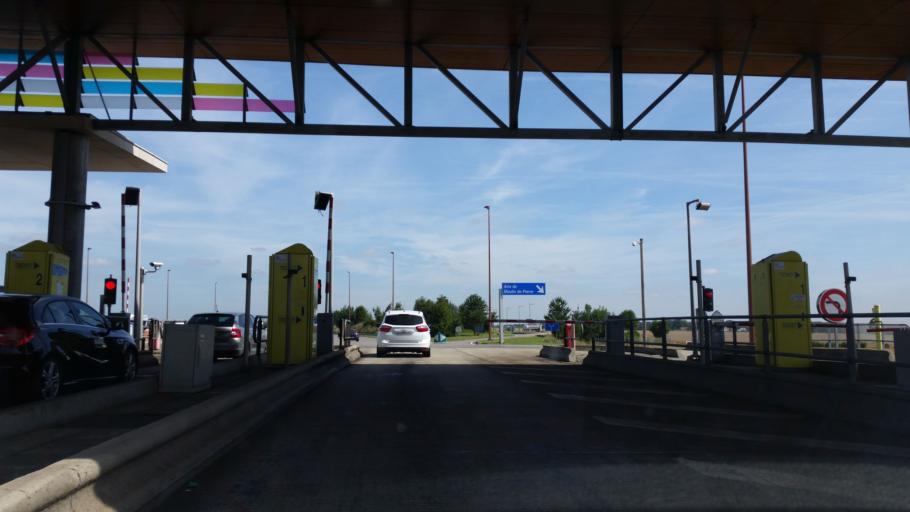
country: FR
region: Haute-Normandie
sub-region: Departement de la Seine-Maritime
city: Aumale
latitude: 49.7593
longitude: 1.7028
